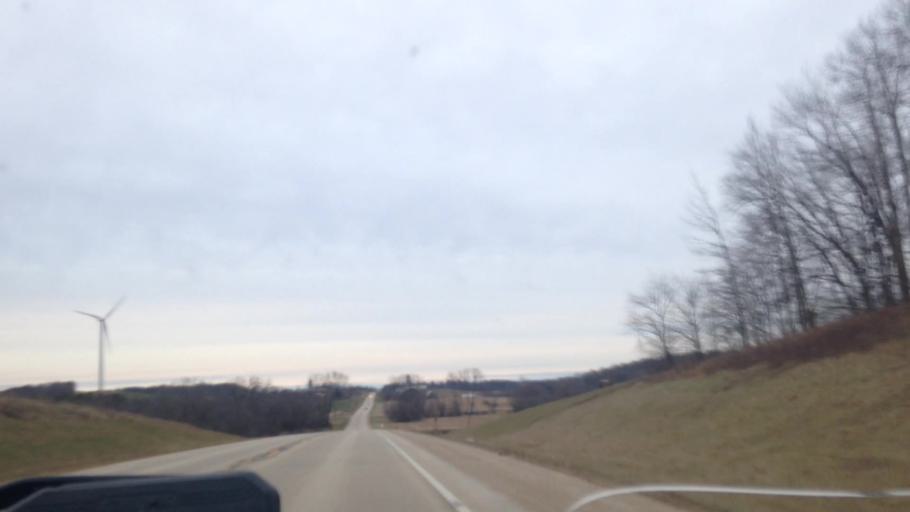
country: US
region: Wisconsin
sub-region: Dodge County
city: Theresa
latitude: 43.4364
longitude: -88.4503
